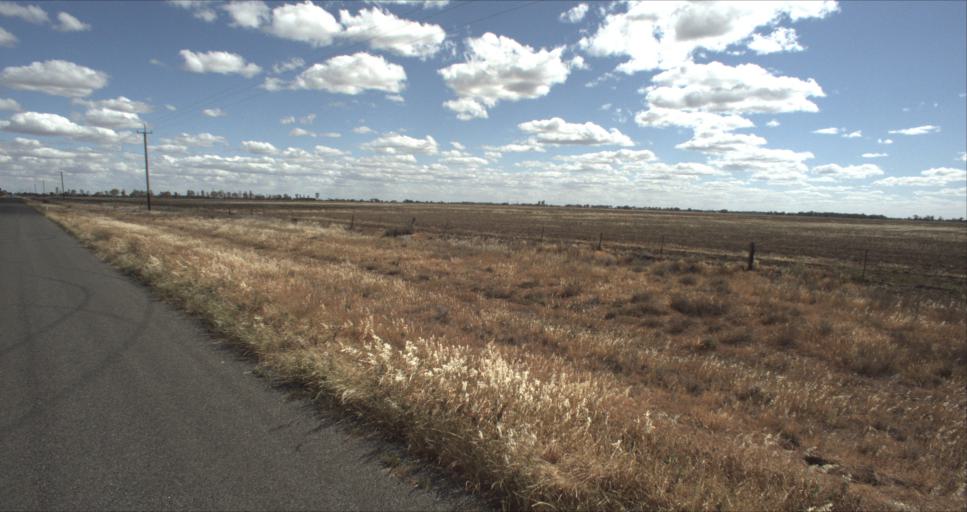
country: AU
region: New South Wales
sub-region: Leeton
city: Leeton
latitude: -34.4313
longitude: 146.2581
